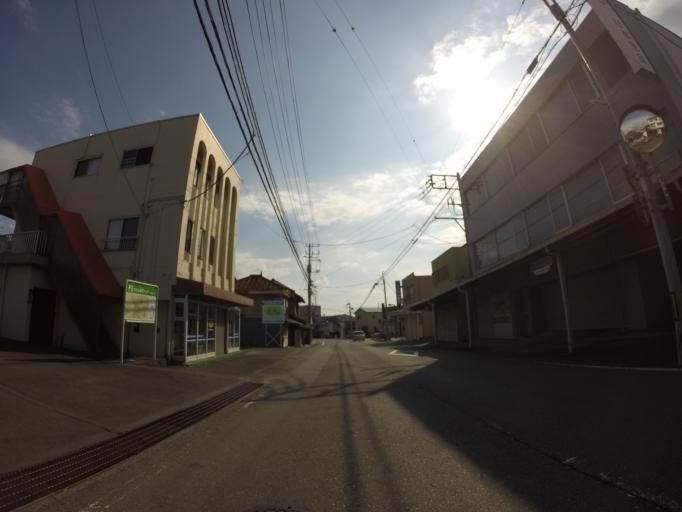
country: JP
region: Shizuoka
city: Fuji
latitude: 35.1863
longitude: 138.6465
